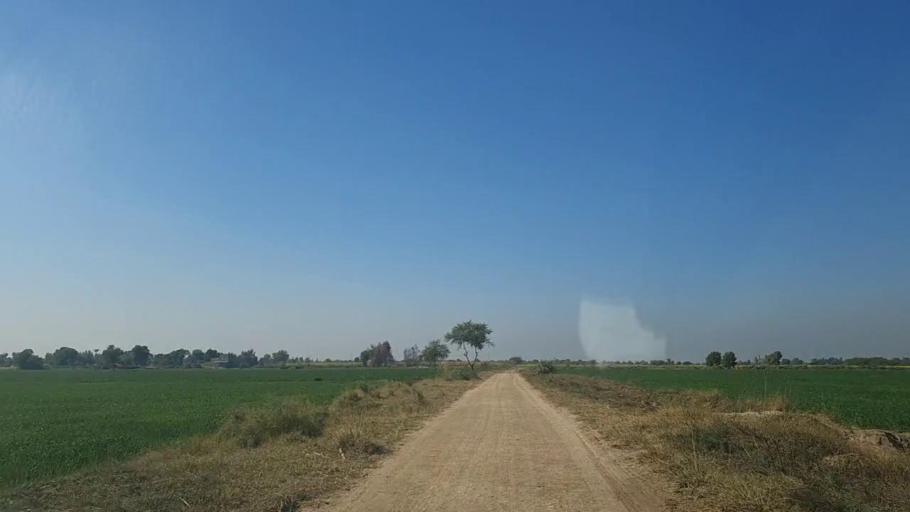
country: PK
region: Sindh
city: Sinjhoro
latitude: 26.1308
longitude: 68.8446
